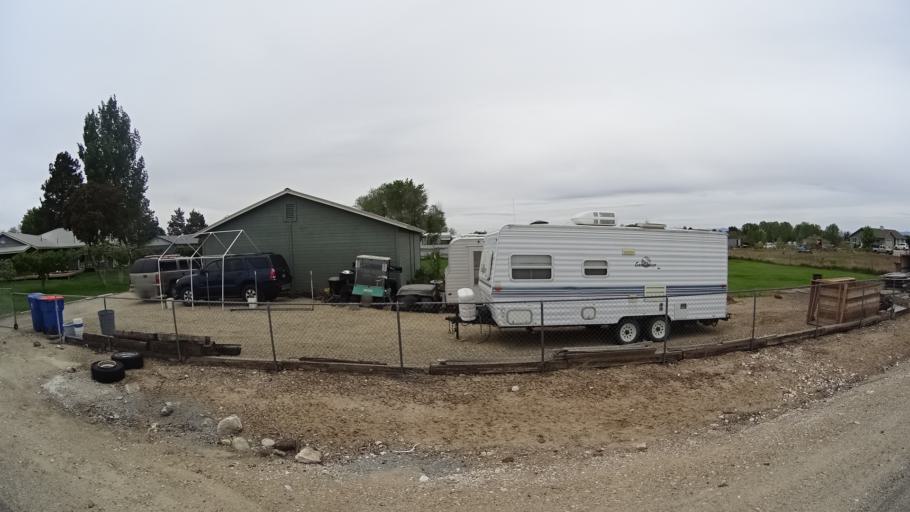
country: US
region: Idaho
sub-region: Ada County
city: Kuna
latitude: 43.4883
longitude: -116.3242
